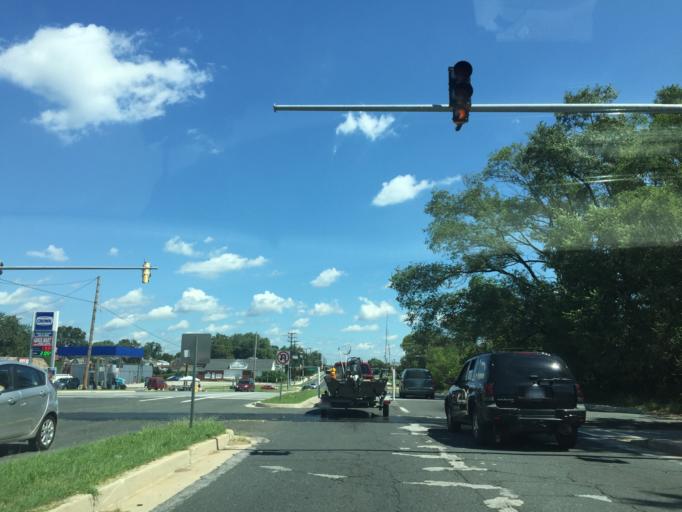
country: US
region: Maryland
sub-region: Baltimore County
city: Dundalk
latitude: 39.2589
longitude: -76.5106
